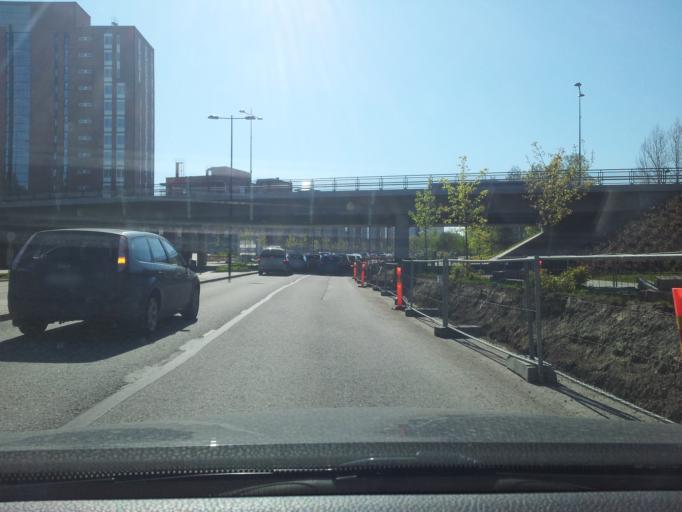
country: FI
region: Uusimaa
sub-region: Helsinki
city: Koukkuniemi
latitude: 60.1662
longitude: 24.7375
